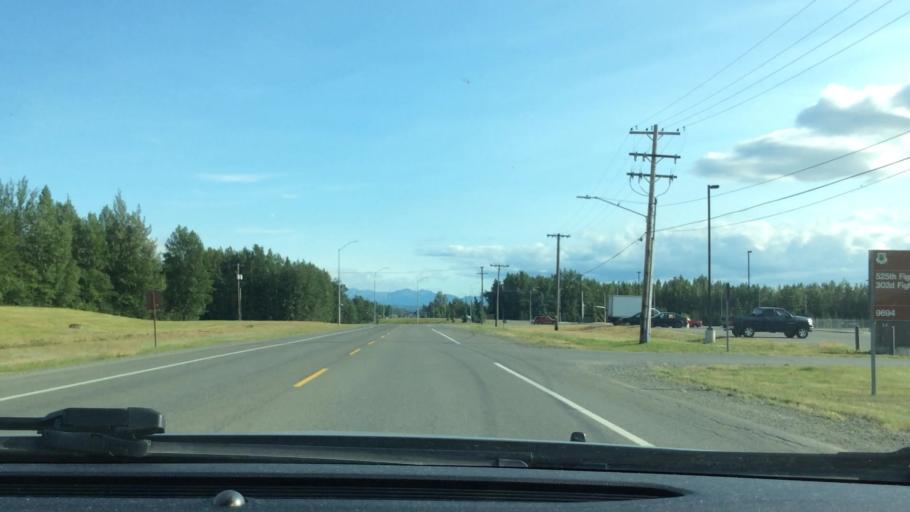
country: US
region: Alaska
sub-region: Anchorage Municipality
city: Anchorage
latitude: 61.2432
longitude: -149.7786
